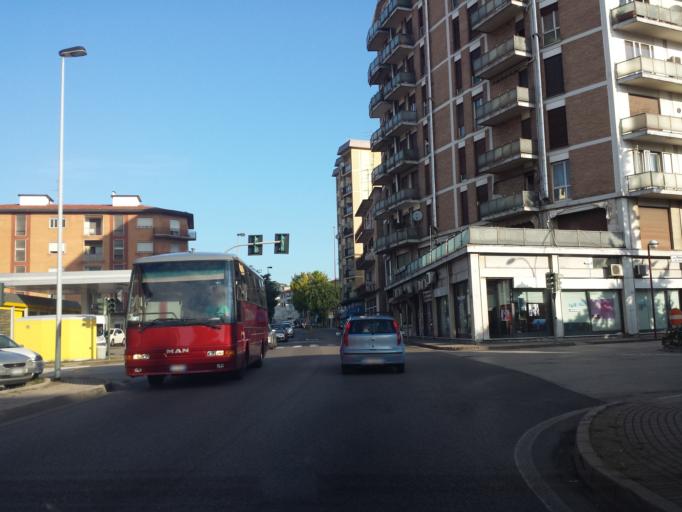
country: IT
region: Veneto
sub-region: Provincia di Vicenza
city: Brendola
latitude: 45.4927
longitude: 11.4339
